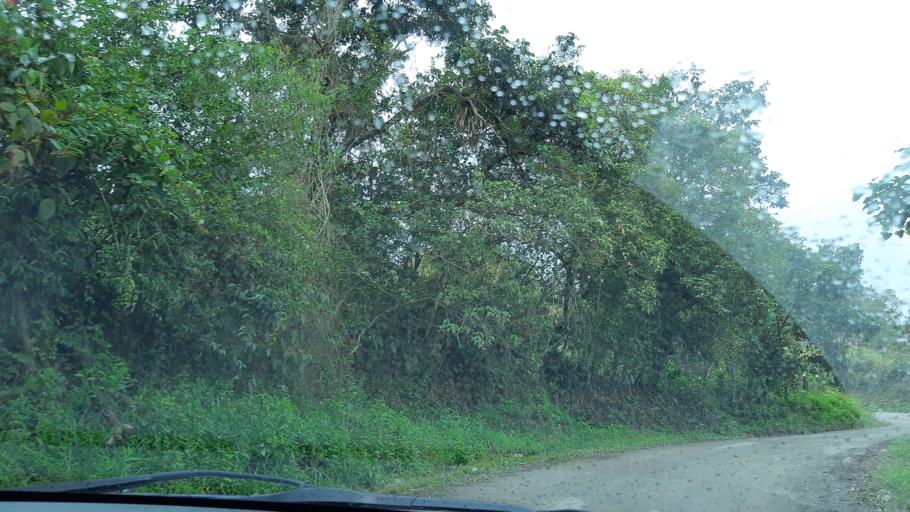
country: CO
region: Boyaca
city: Chivor
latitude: 4.9611
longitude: -73.3187
